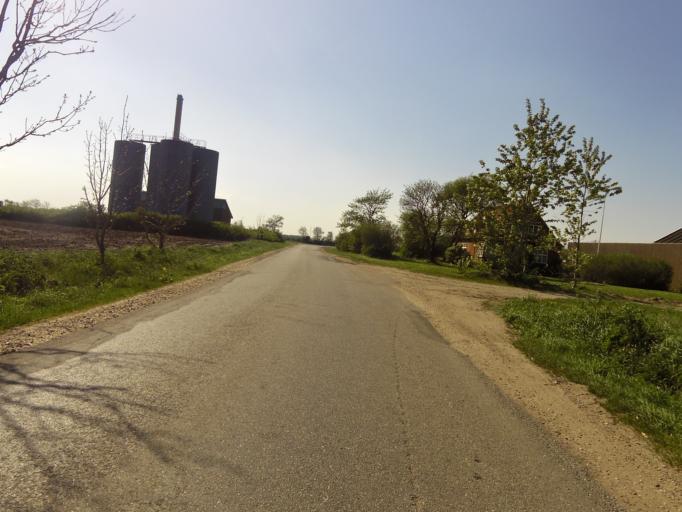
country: DK
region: South Denmark
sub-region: Tonder Kommune
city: Sherrebek
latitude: 55.2220
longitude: 8.8348
